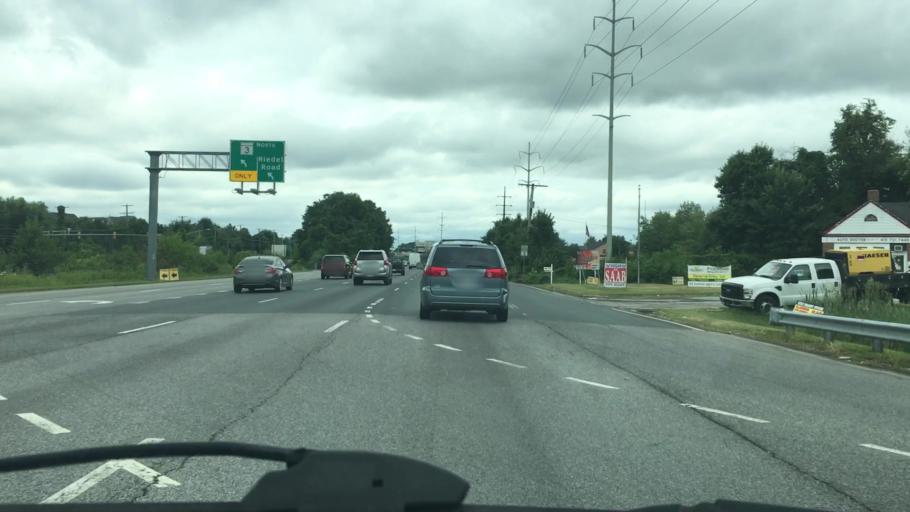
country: US
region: Maryland
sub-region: Anne Arundel County
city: Gambrills
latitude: 39.0391
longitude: -76.6755
